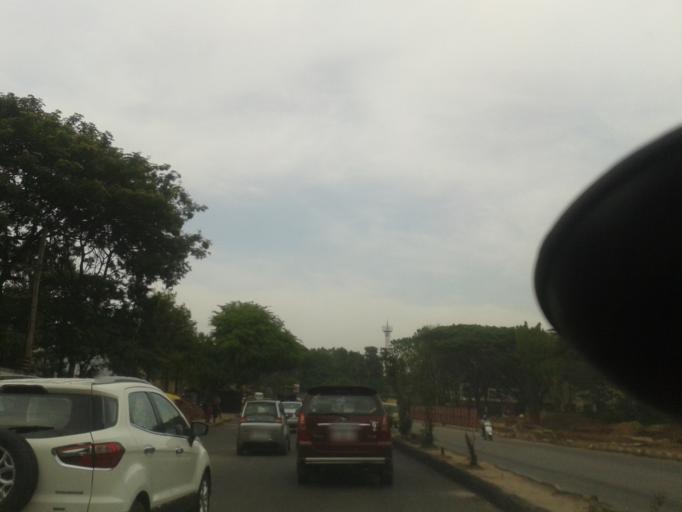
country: IN
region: Karnataka
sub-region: Bangalore Urban
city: Bangalore
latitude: 12.9364
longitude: 77.5185
